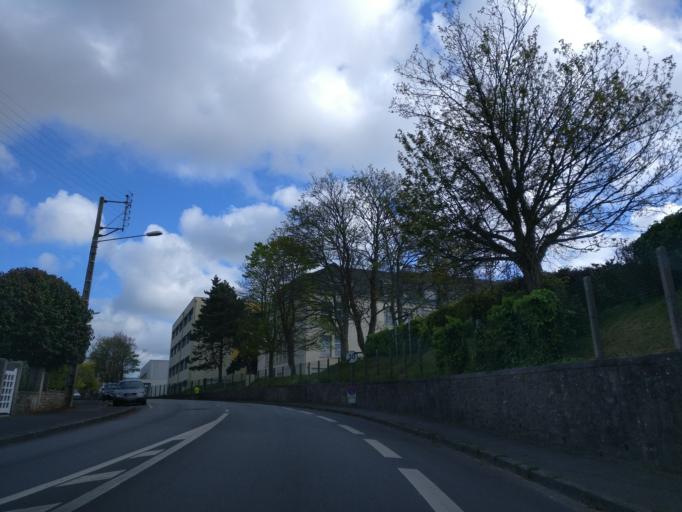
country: FR
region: Brittany
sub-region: Departement du Finistere
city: Brest
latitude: 48.4040
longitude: -4.4580
